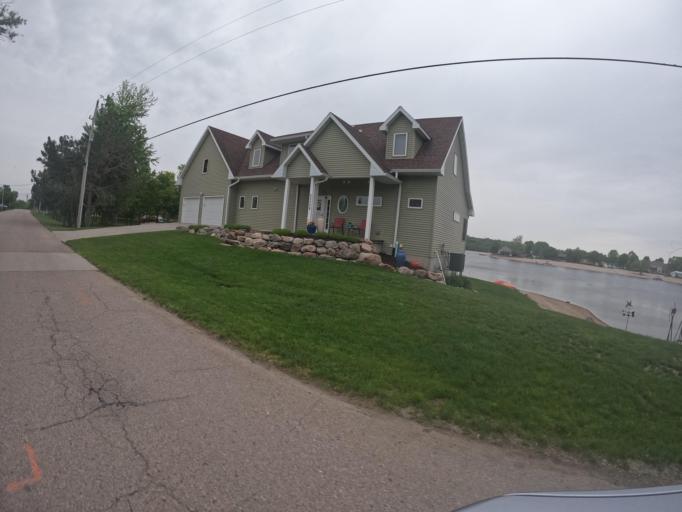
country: US
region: Nebraska
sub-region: Sarpy County
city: Offutt Air Force Base
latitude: 41.0547
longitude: -95.9520
